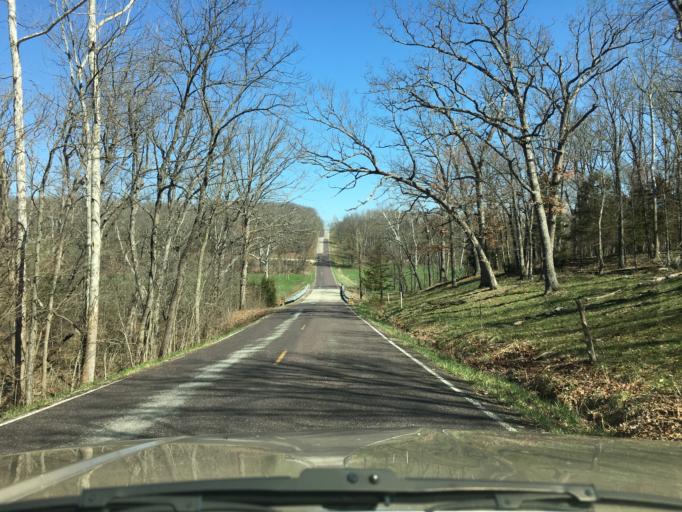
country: US
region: Missouri
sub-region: Franklin County
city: New Haven
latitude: 38.5461
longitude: -91.3303
